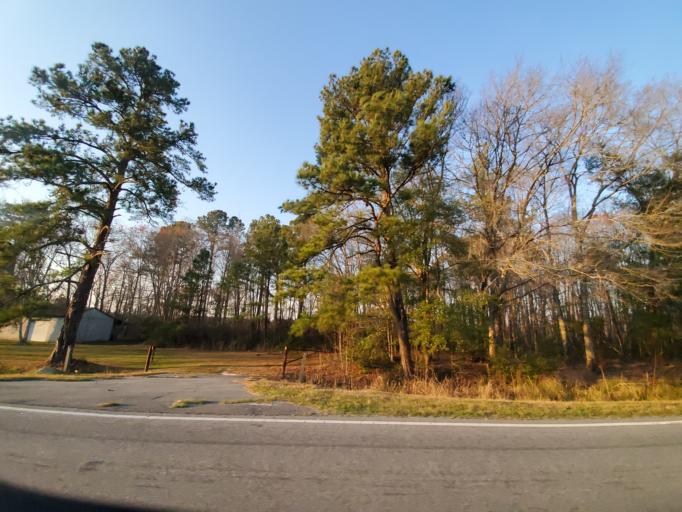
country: US
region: South Carolina
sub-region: Dorchester County
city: Ridgeville
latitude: 33.0518
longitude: -80.4761
